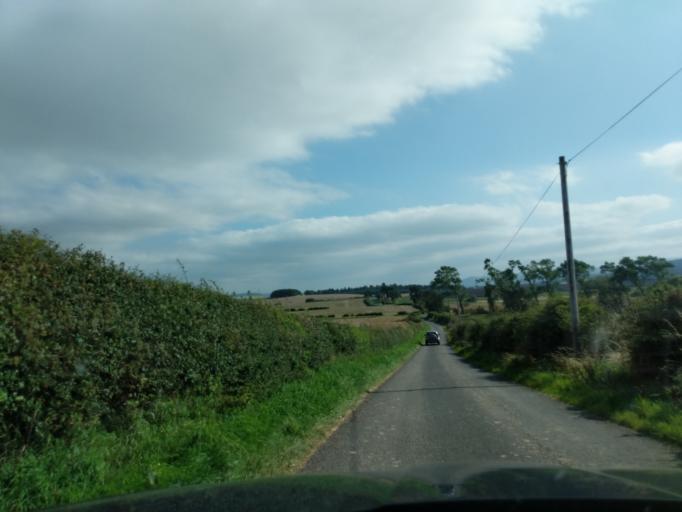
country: GB
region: England
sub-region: Northumberland
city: Ford
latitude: 55.6533
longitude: -2.1463
